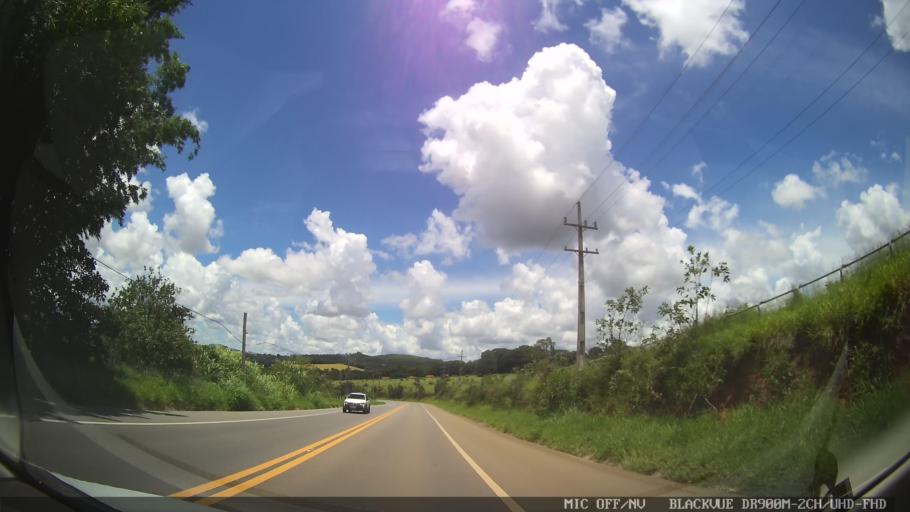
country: BR
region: Sao Paulo
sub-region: Braganca Paulista
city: Braganca Paulista
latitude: -22.8926
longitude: -46.6048
